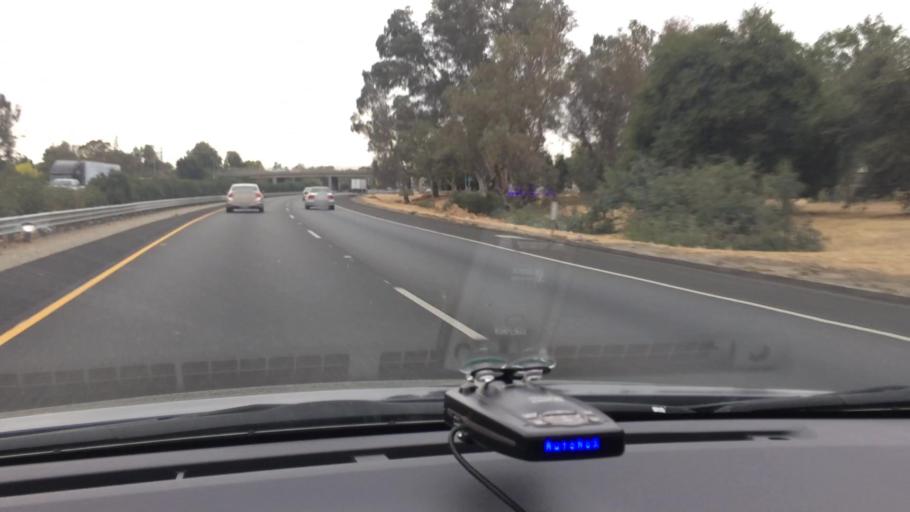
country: US
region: California
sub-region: San Joaquin County
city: Lodi
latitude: 38.1430
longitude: -121.2604
